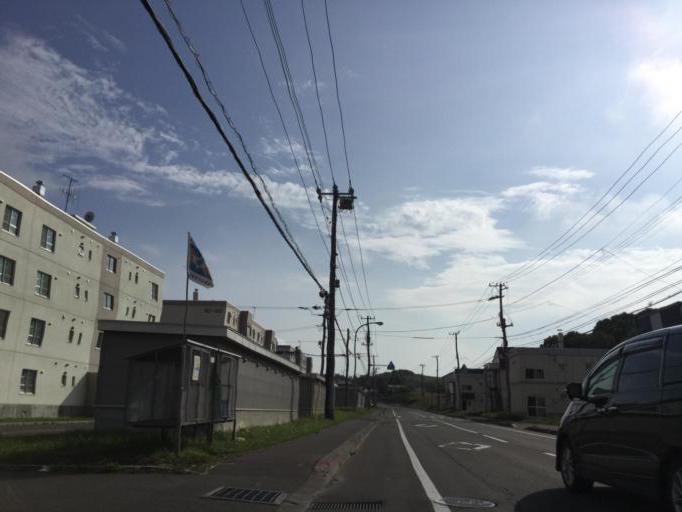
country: JP
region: Hokkaido
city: Wakkanai
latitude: 45.3870
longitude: 141.6753
